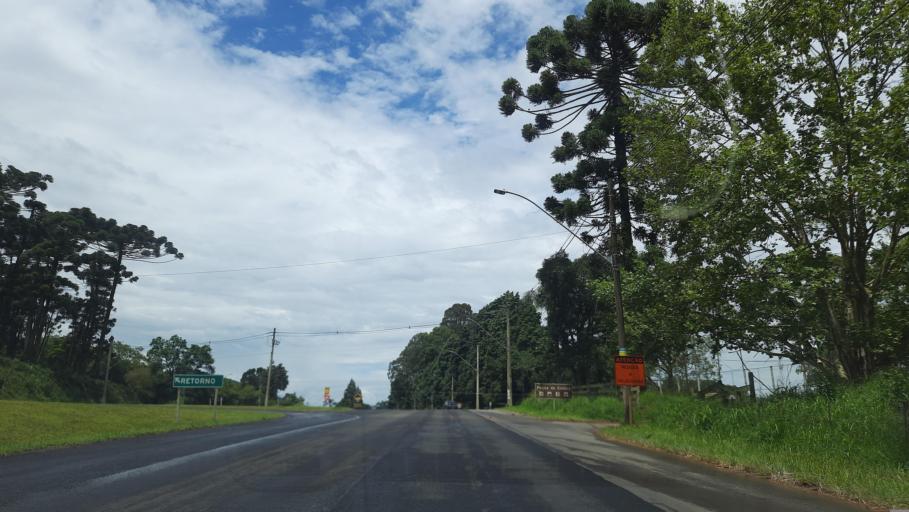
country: BR
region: Minas Gerais
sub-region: Pocos De Caldas
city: Pocos de Caldas
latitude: -21.7973
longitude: -46.6460
